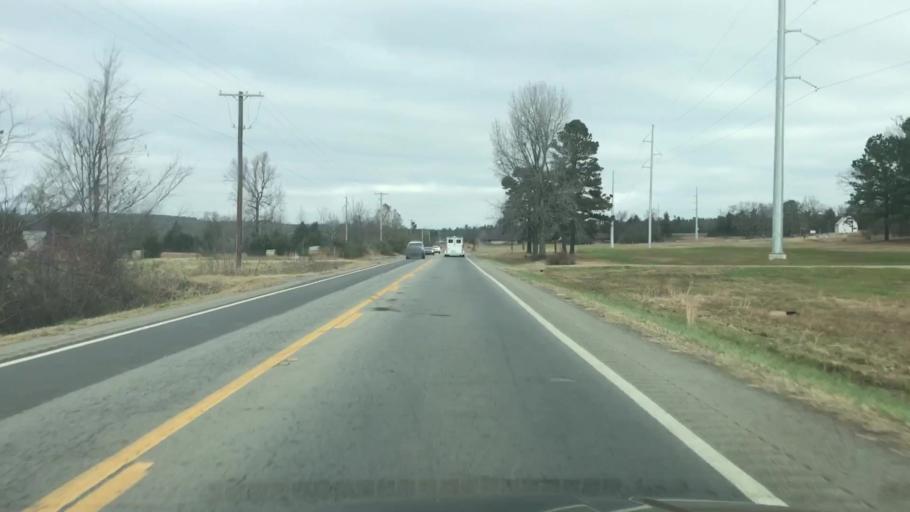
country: US
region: Arkansas
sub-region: Scott County
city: Waldron
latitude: 34.9430
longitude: -94.1030
